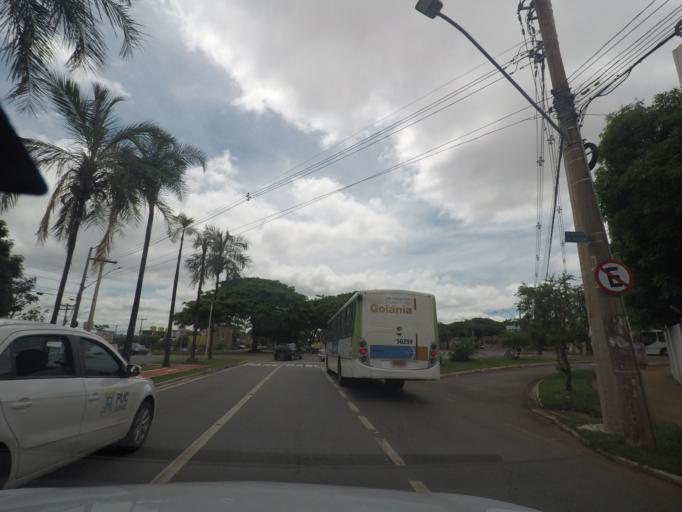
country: BR
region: Goias
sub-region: Goiania
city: Goiania
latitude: -16.6751
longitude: -49.2374
